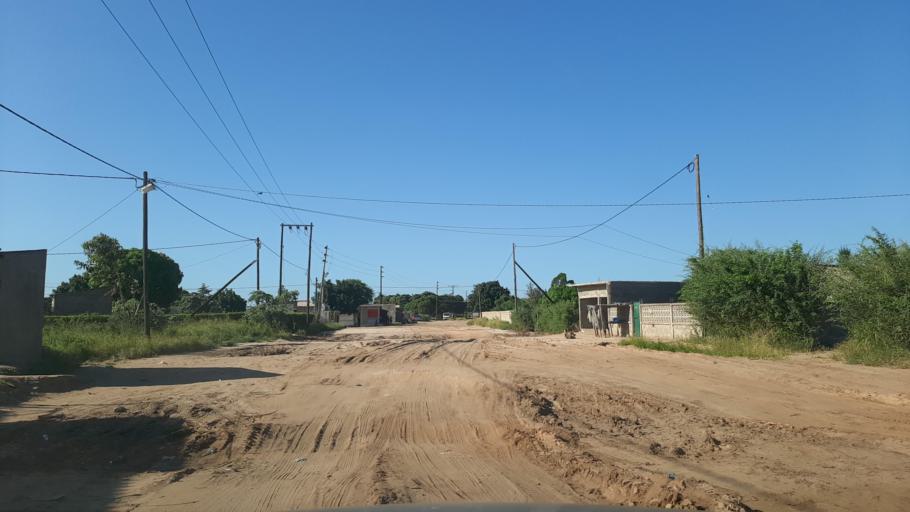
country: MZ
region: Maputo City
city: Maputo
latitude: -25.7635
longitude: 32.5473
